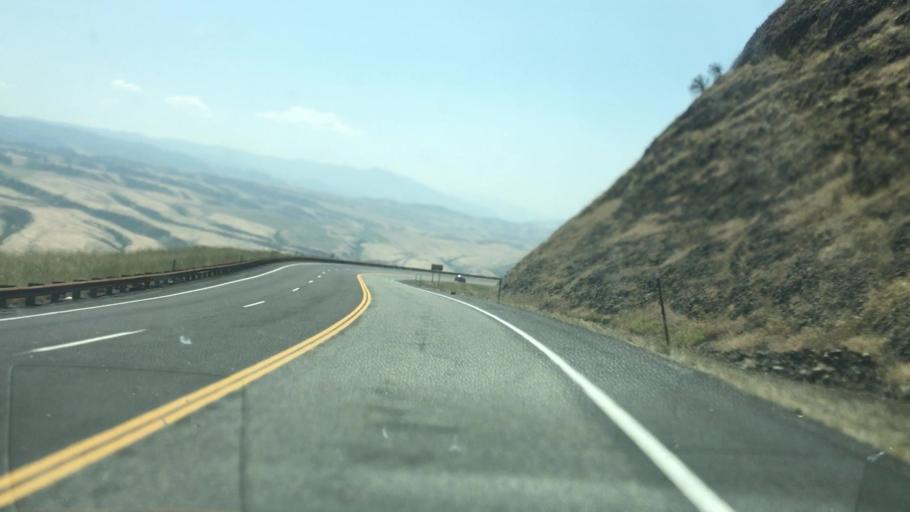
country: US
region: Idaho
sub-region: Idaho County
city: Grangeville
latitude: 45.8093
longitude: -116.2812
